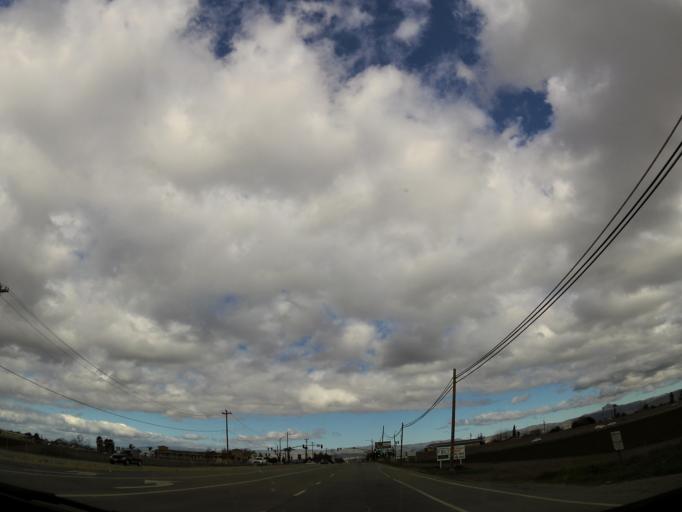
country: US
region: California
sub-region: San Benito County
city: Hollister
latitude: 36.8635
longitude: -121.4014
